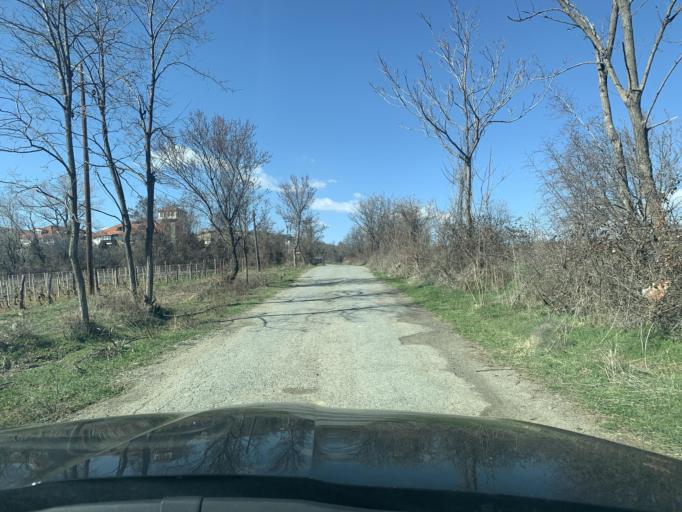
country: MK
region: Demir Kapija
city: Demir Kapija
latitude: 41.4101
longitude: 22.2287
